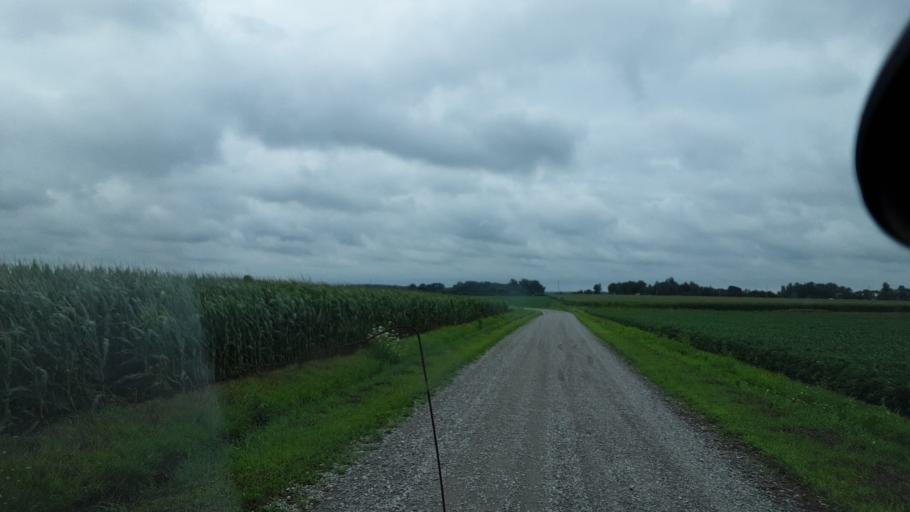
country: US
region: Indiana
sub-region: Wells County
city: Ossian
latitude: 40.8395
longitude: -85.0819
